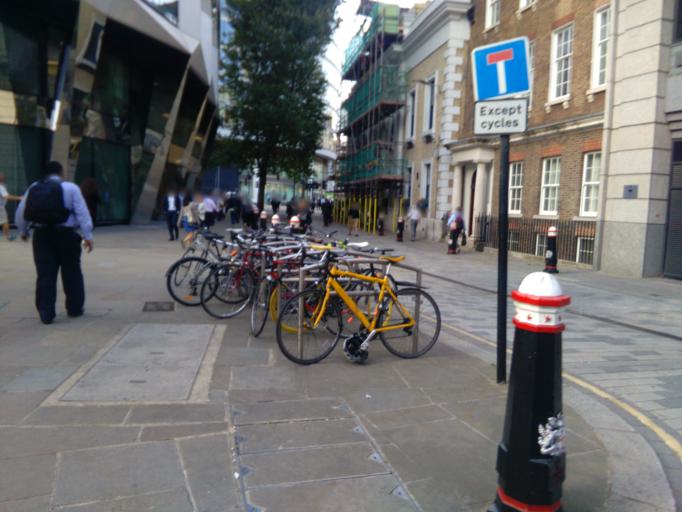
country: GB
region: England
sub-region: Greater London
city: City of London
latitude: 51.5168
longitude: -0.0895
